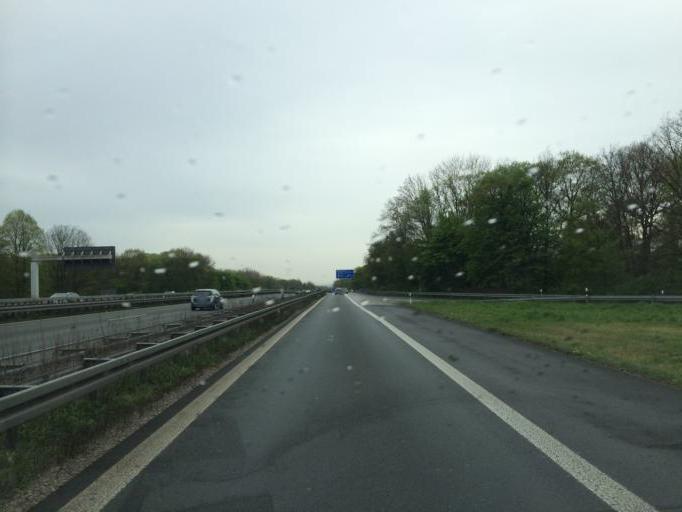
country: DE
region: North Rhine-Westphalia
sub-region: Regierungsbezirk Munster
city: Recklinghausen
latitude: 51.5851
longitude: 7.1884
